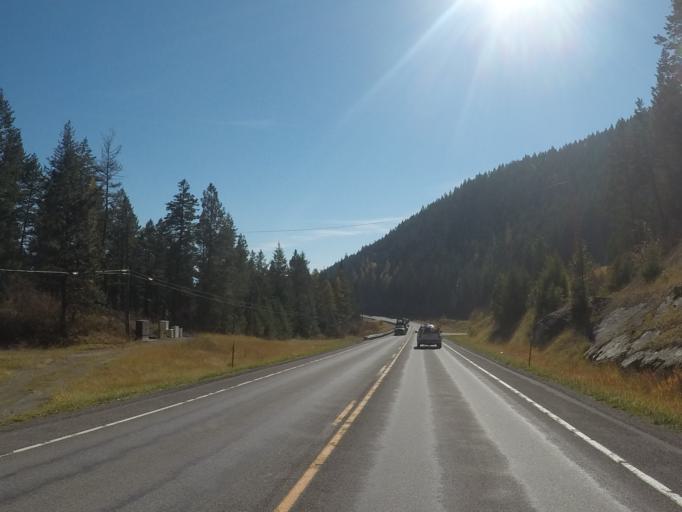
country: US
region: Montana
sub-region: Flathead County
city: Lakeside
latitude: 47.9727
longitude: -114.1970
